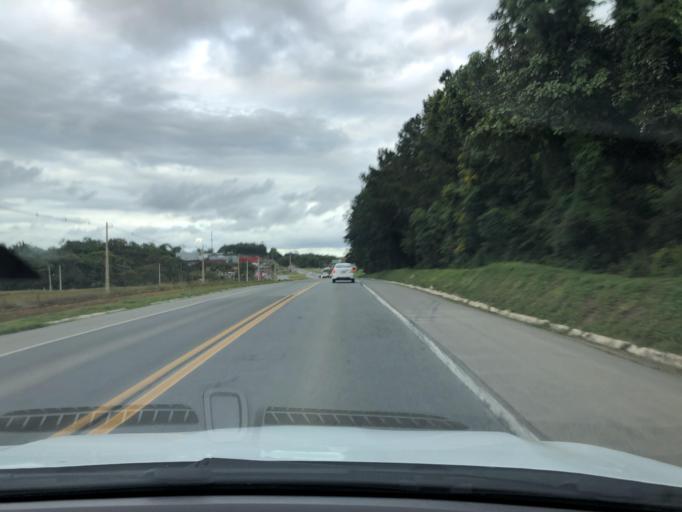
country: BR
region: Santa Catarina
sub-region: Joinville
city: Joinville
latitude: -26.4273
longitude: -48.7906
